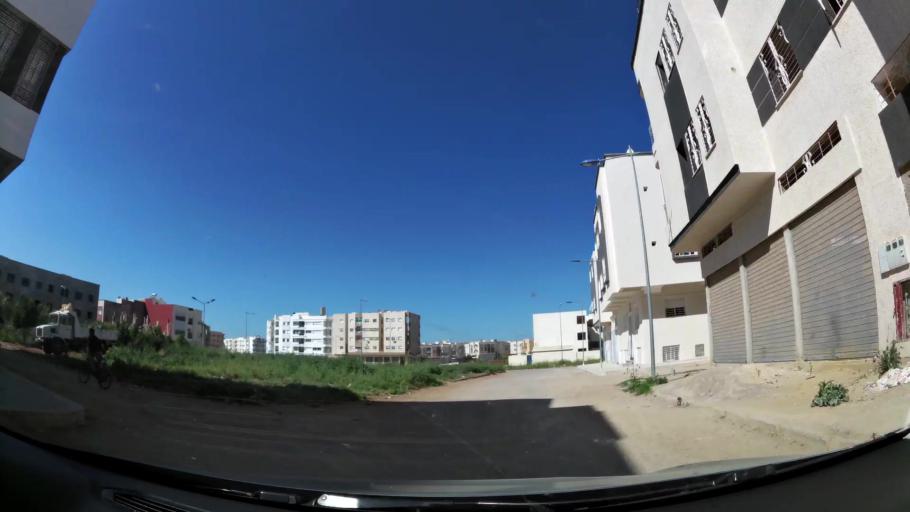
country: MA
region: Fes-Boulemane
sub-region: Fes
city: Fes
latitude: 33.9958
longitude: -5.0101
